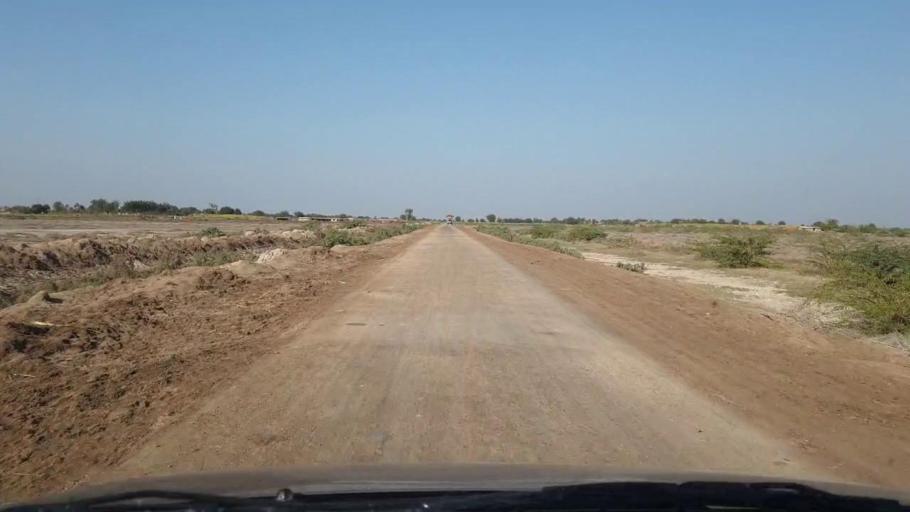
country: PK
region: Sindh
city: Digri
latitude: 25.1399
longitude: 69.2809
